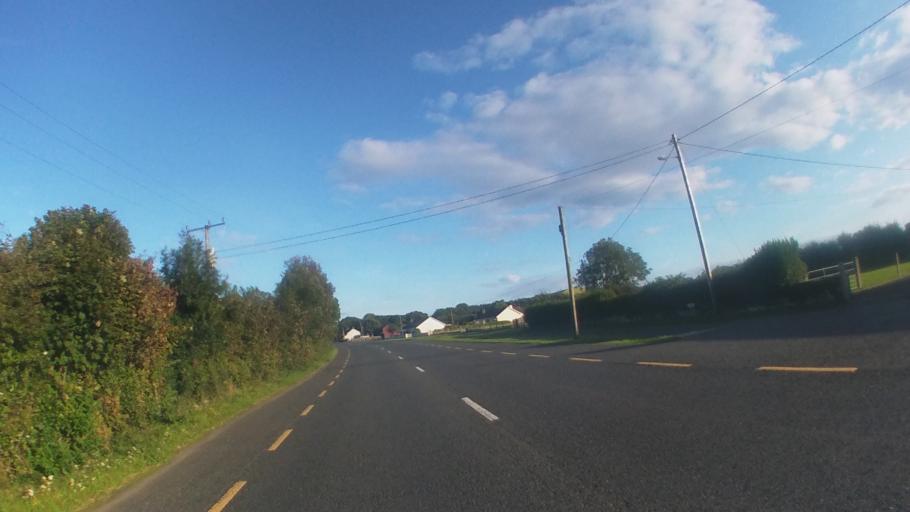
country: IE
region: Leinster
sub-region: Lu
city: Carlingford
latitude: 54.0274
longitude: -6.1546
